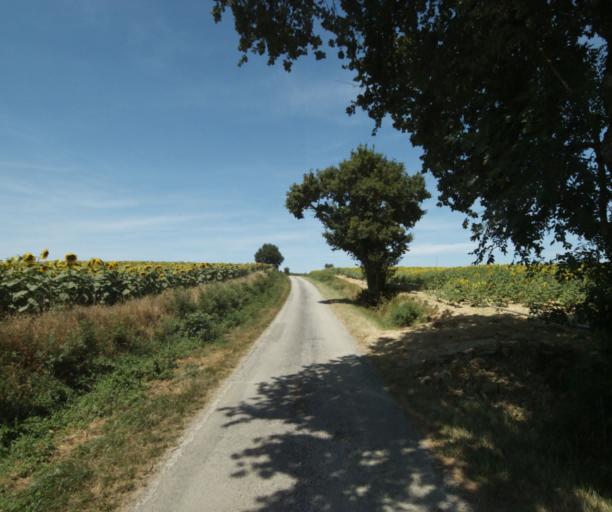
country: FR
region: Midi-Pyrenees
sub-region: Departement de la Haute-Garonne
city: Revel
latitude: 43.4950
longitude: 2.0341
